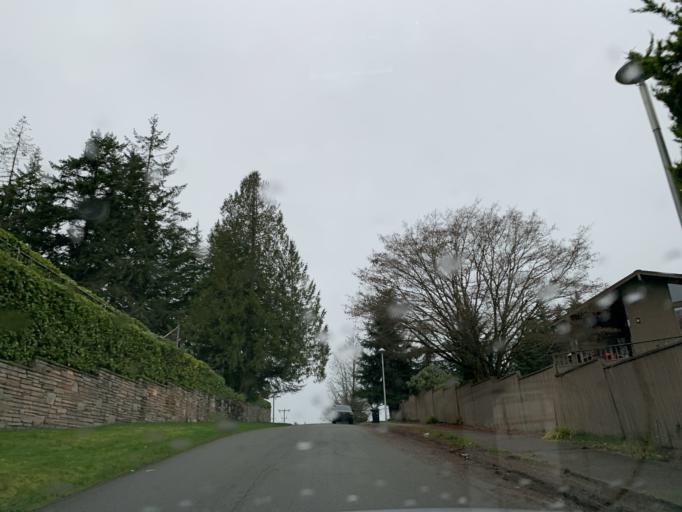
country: US
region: Washington
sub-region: King County
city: Yarrow Point
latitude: 47.6649
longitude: -122.2731
